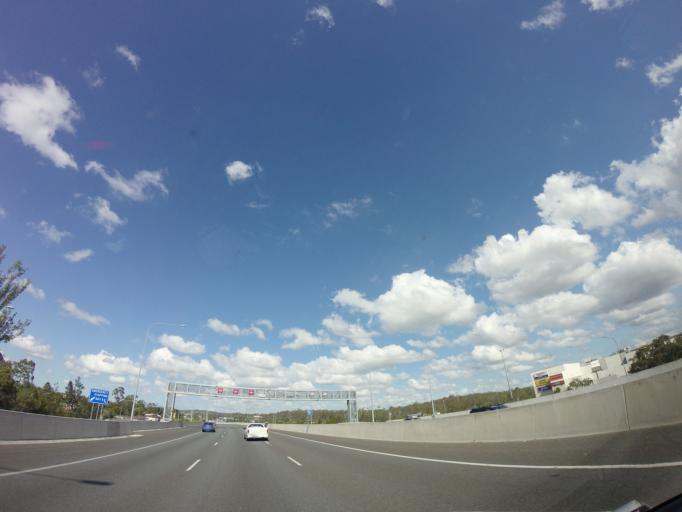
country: AU
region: Queensland
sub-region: Ipswich
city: Redbank
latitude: -27.6039
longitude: 152.8676
